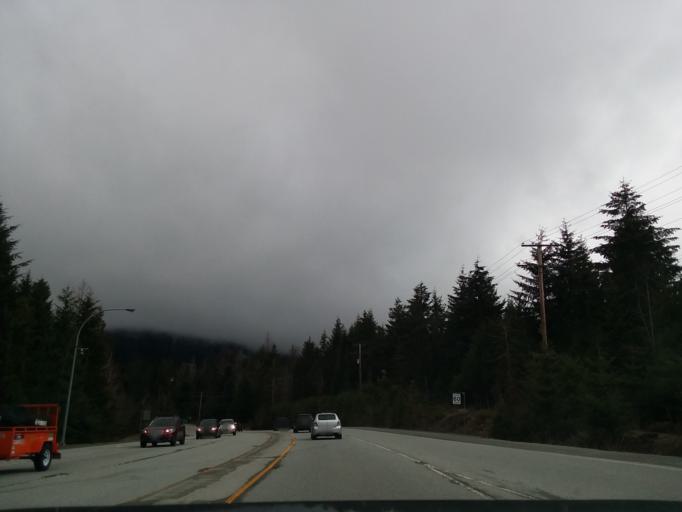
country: CA
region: British Columbia
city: Whistler
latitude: 50.1215
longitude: -122.9607
